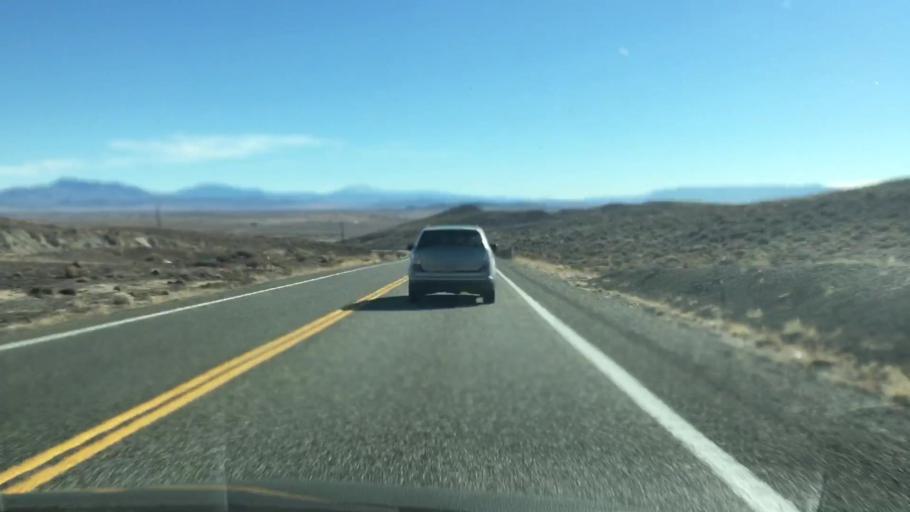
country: US
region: Nevada
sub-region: Lyon County
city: Yerington
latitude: 39.1748
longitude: -119.2058
